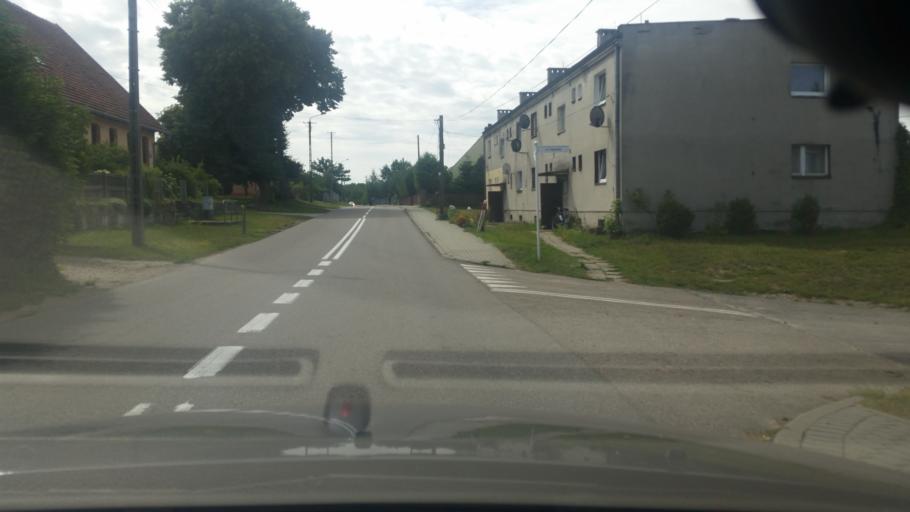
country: PL
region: Pomeranian Voivodeship
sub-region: Powiat leborski
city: Leba
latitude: 54.7508
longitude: 17.6661
